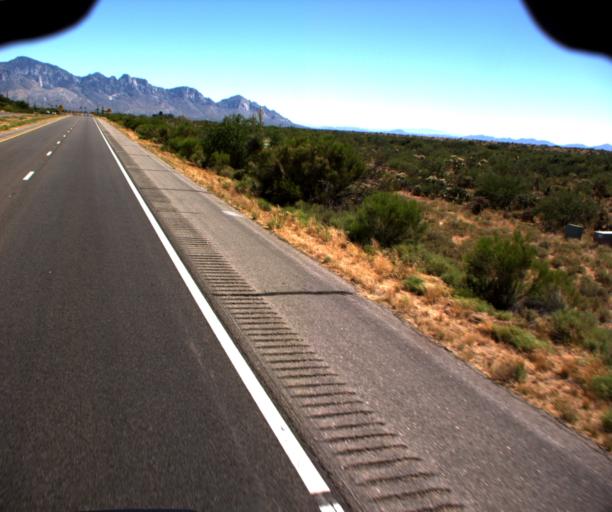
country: US
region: Arizona
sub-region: Pima County
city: Catalina
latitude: 32.5287
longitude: -110.9293
